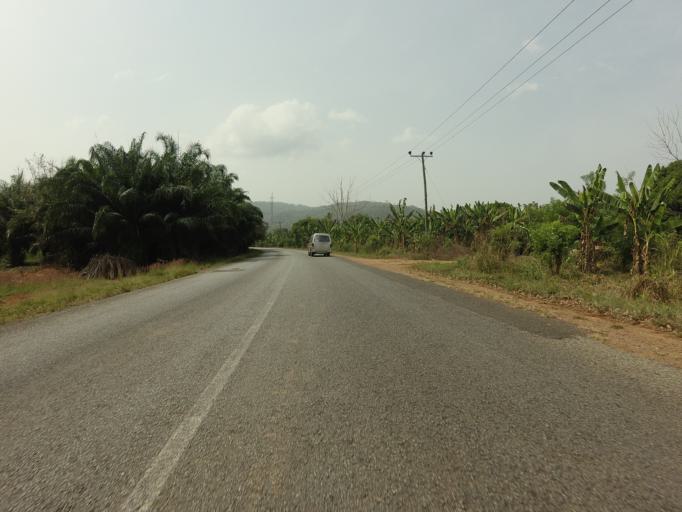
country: GH
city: Akropong
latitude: 6.2991
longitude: 0.1349
